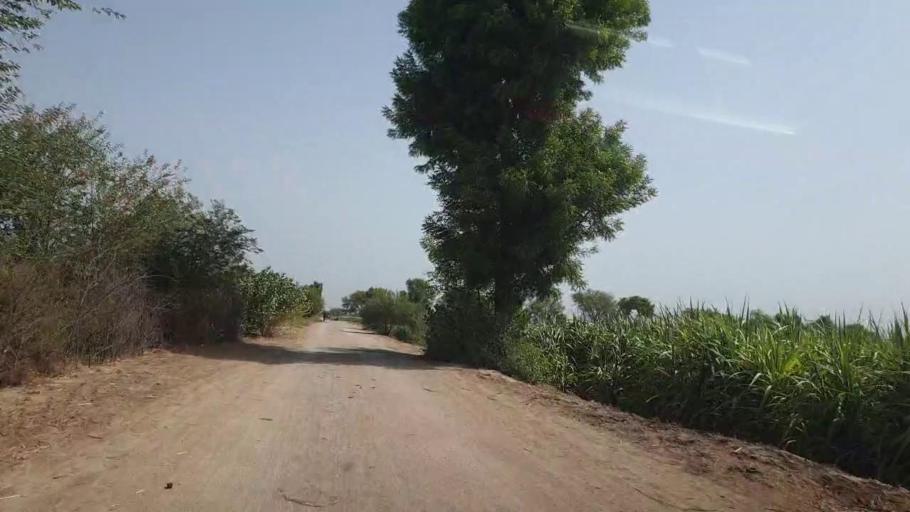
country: PK
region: Sindh
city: Daur
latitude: 26.3157
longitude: 68.2155
